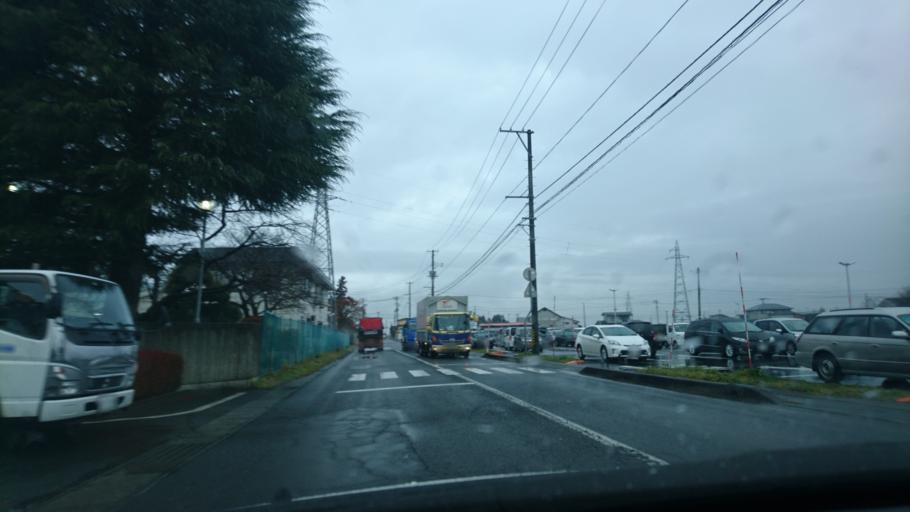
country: JP
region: Iwate
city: Kitakami
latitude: 39.2956
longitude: 141.0547
